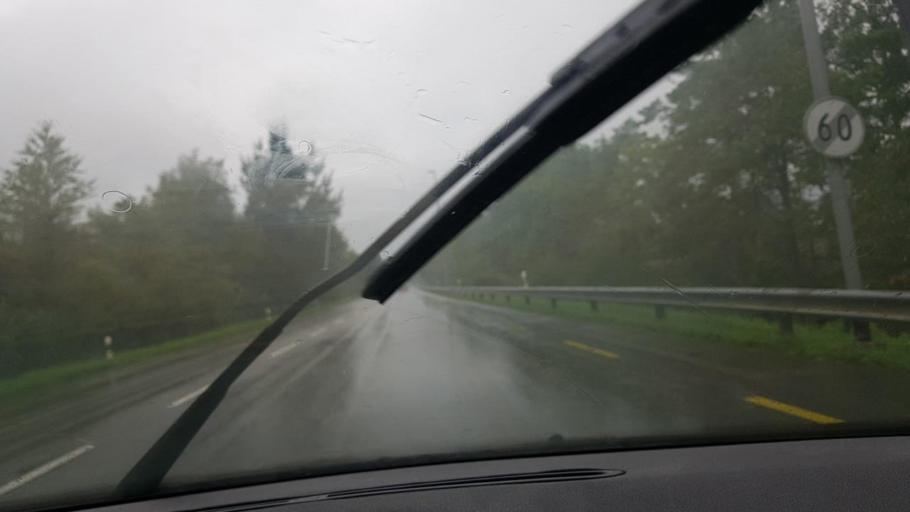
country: LI
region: Triesen
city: Triesen
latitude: 47.0878
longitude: 9.5195
